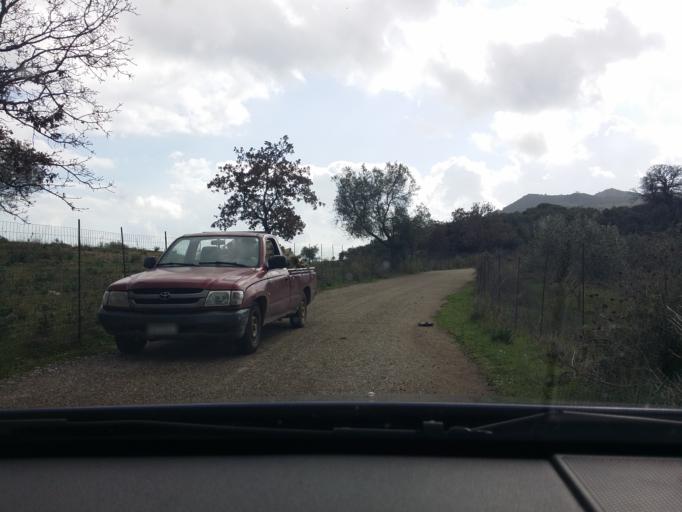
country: GR
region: West Greece
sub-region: Nomos Aitolias kai Akarnanias
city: Fitiai
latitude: 38.6700
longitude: 21.1904
